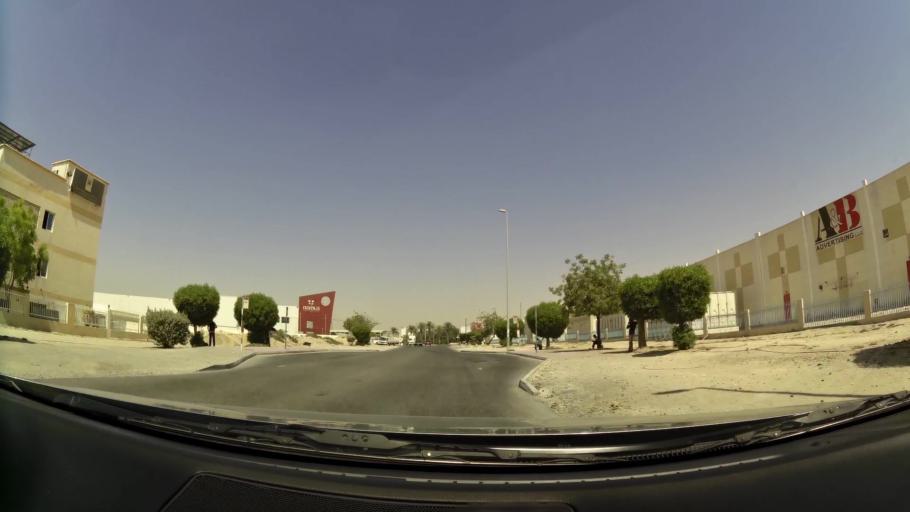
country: AE
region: Dubai
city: Dubai
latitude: 24.9705
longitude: 55.1702
